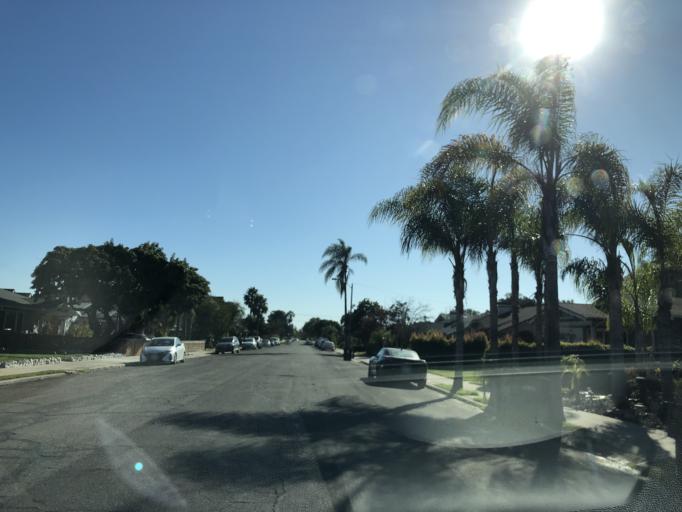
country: US
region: California
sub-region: San Diego County
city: San Diego
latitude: 32.7435
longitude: -117.1272
